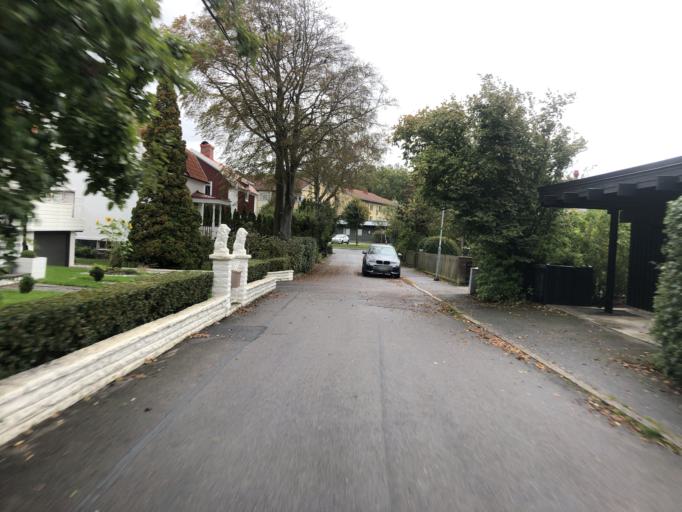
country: SE
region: Vaestra Goetaland
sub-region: Molndal
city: Moelndal
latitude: 57.6587
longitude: 12.0072
